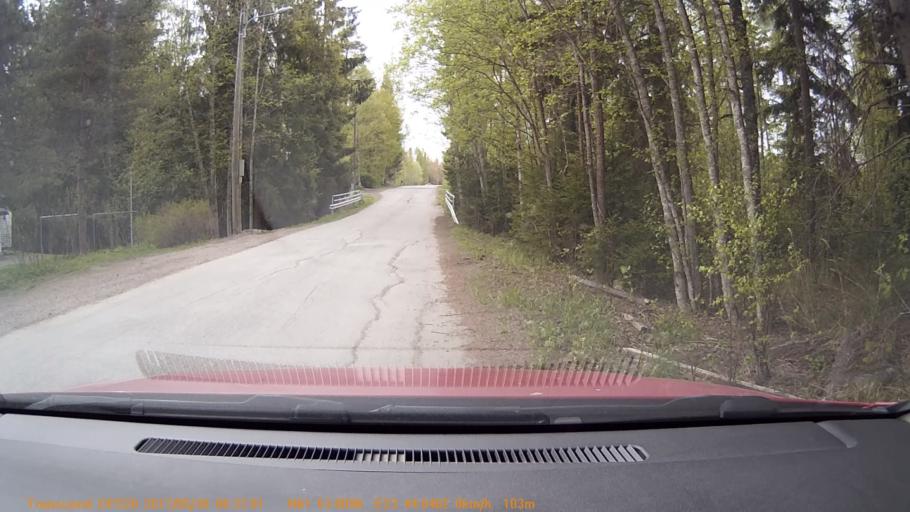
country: FI
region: Pirkanmaa
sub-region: Tampere
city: Kuru
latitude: 61.8835
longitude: 23.7341
